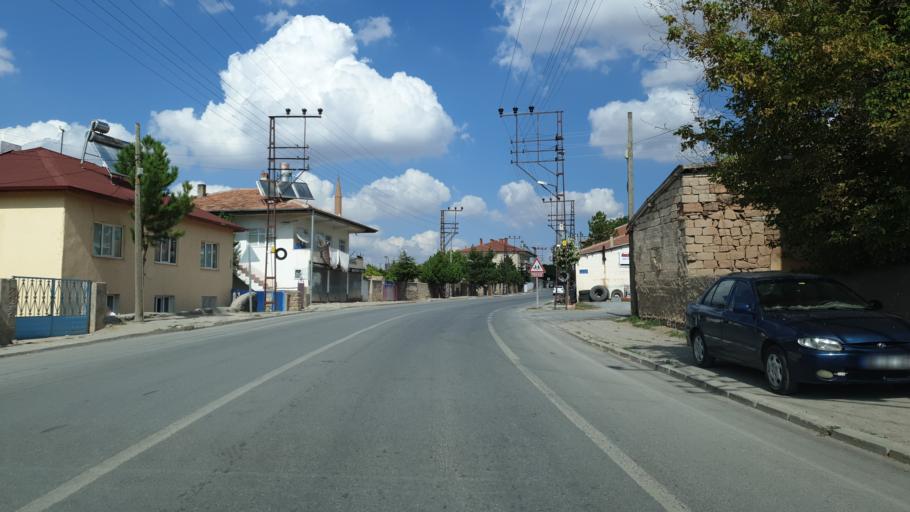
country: TR
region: Kayseri
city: Felahiye
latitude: 39.0889
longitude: 35.5649
